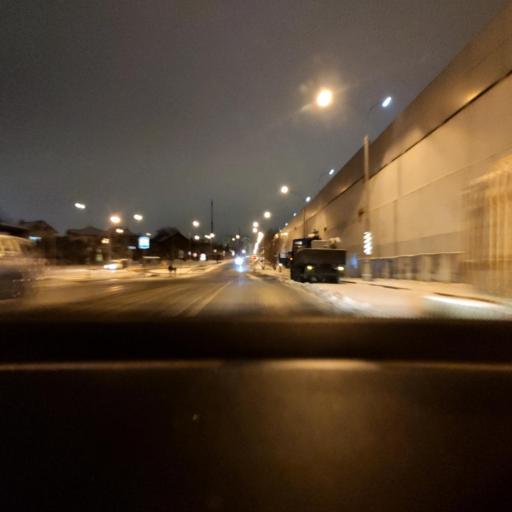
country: RU
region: Moskovskaya
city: Pavshino
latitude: 55.8649
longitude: 37.3659
